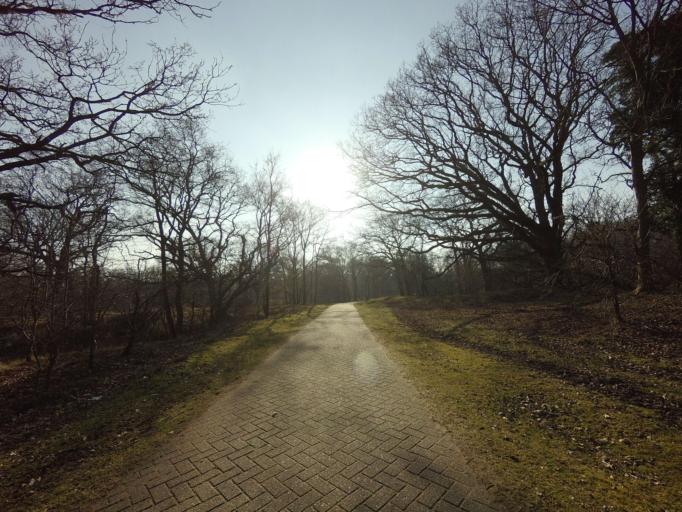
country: NL
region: North Holland
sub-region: Gemeente Bloemendaal
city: Bloemendaal
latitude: 52.4034
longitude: 4.5954
